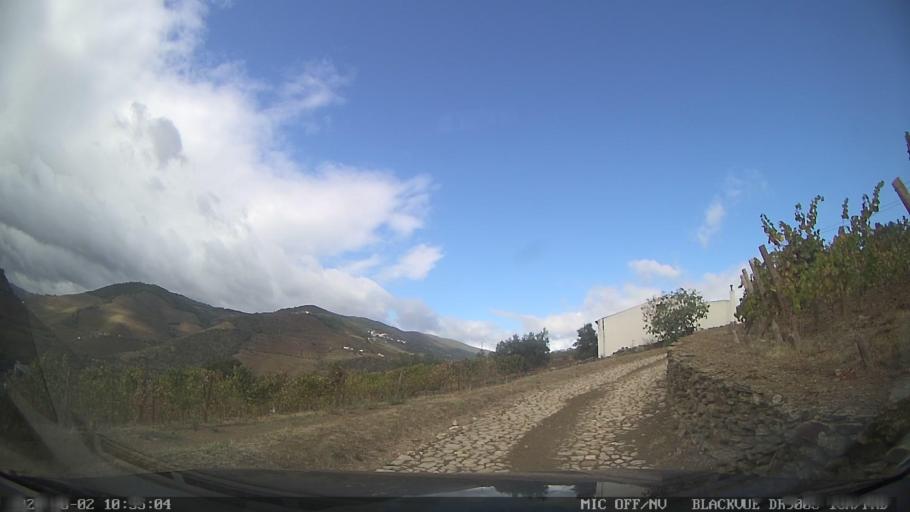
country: PT
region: Vila Real
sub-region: Sabrosa
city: Vilela
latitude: 41.1915
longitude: -7.5370
